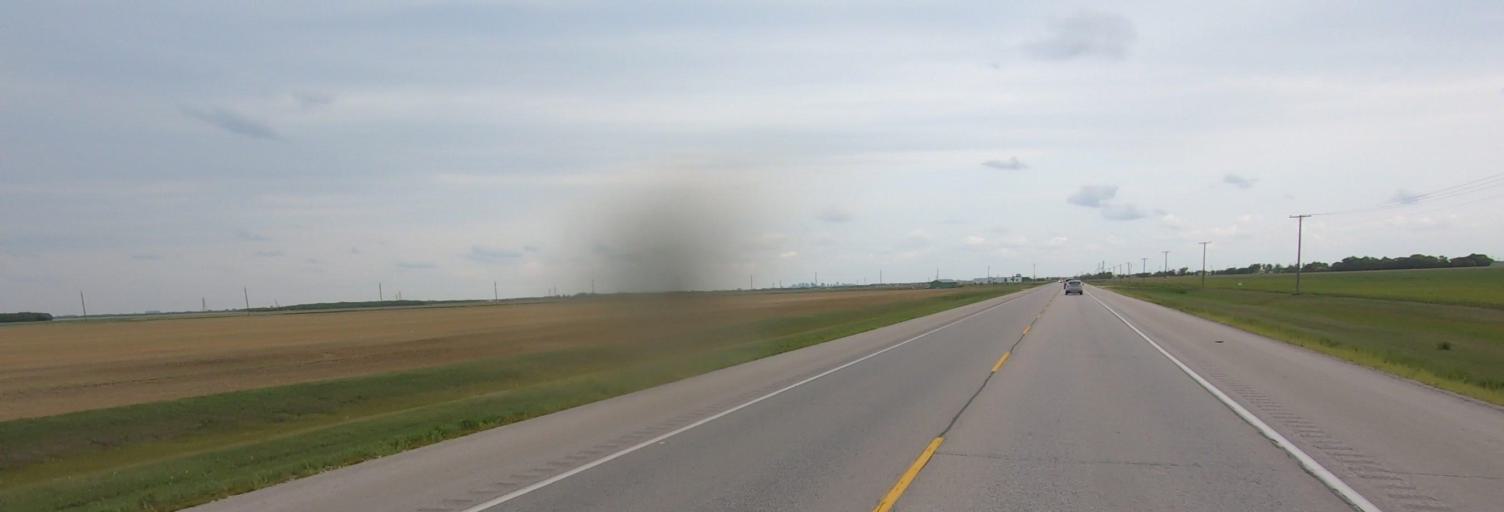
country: CA
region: Manitoba
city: Winnipeg
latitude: 49.7938
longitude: -97.2726
